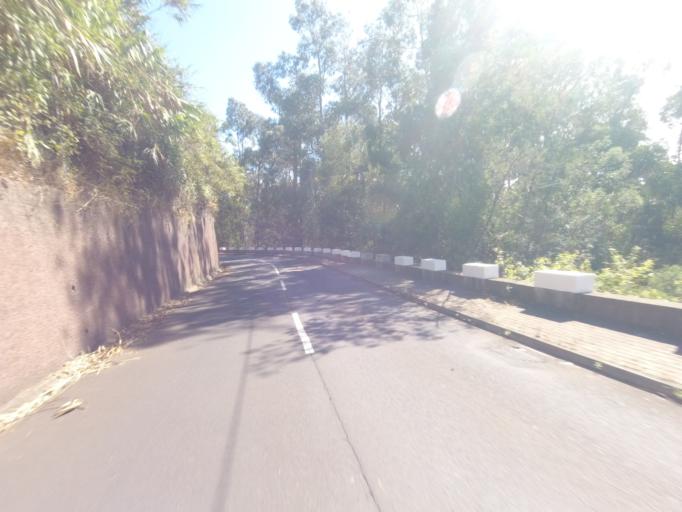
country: PT
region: Madeira
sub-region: Ribeira Brava
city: Campanario
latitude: 32.6852
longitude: -17.0408
